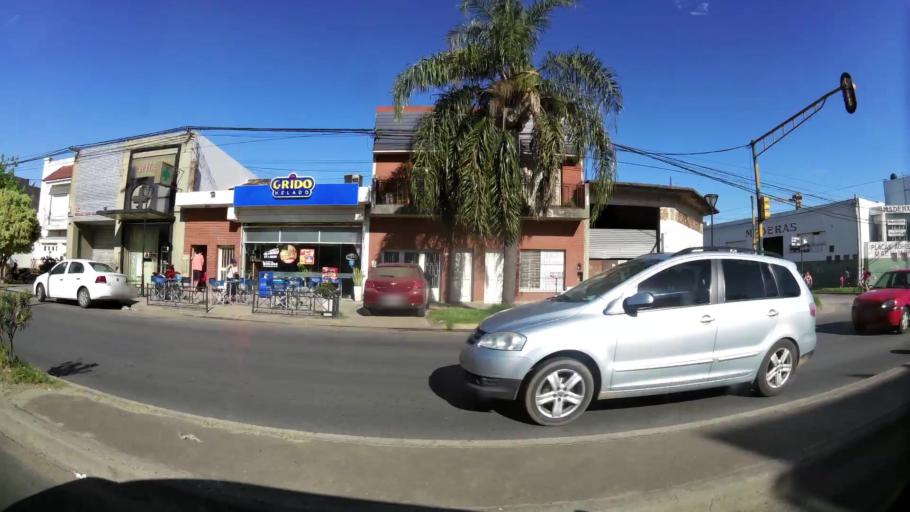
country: AR
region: Santa Fe
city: Santa Fe de la Vera Cruz
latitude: -31.6064
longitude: -60.7035
